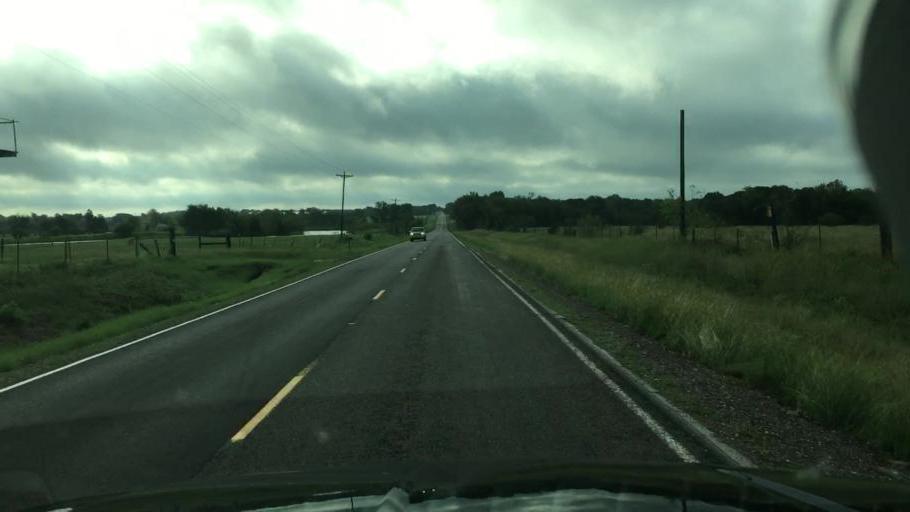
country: US
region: Texas
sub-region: Lee County
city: Lexington
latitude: 30.3727
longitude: -96.8441
